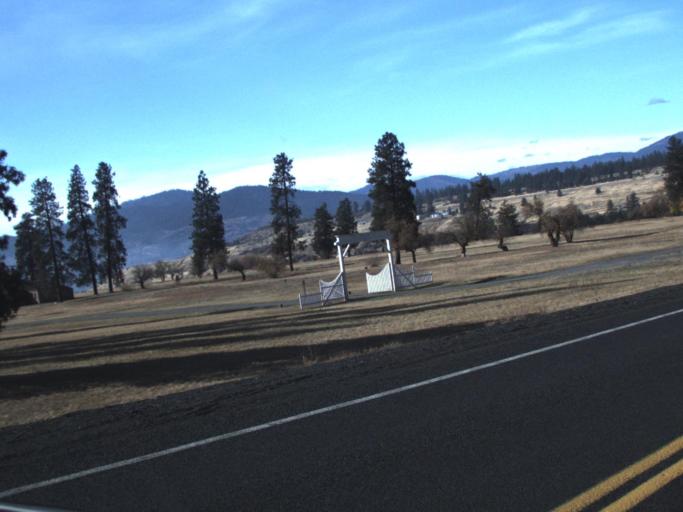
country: US
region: Washington
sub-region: Lincoln County
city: Davenport
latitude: 47.9042
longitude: -118.3040
